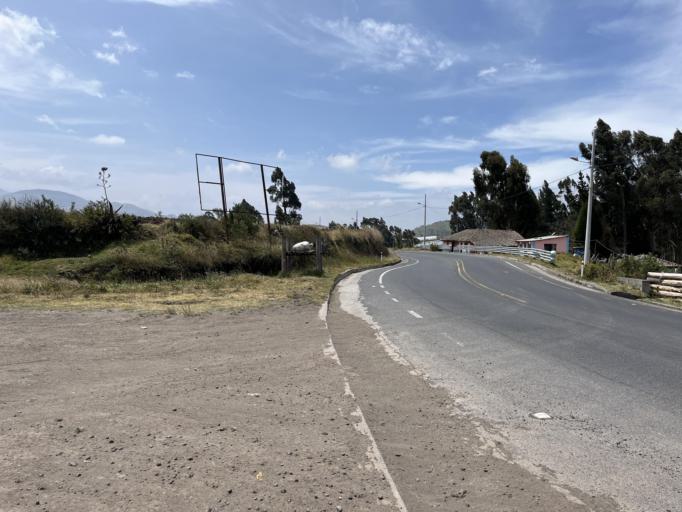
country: EC
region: Pichincha
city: Cayambe
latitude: 0.1624
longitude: -78.0829
